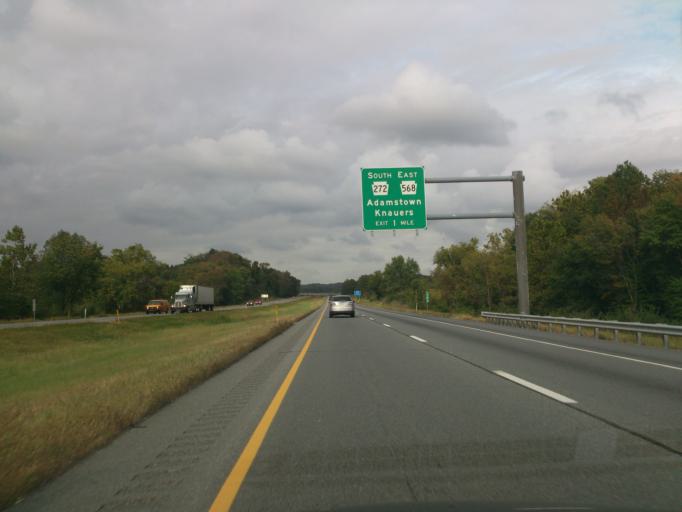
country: US
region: Pennsylvania
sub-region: Lancaster County
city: Adamstown
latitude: 40.2333
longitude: -76.0483
